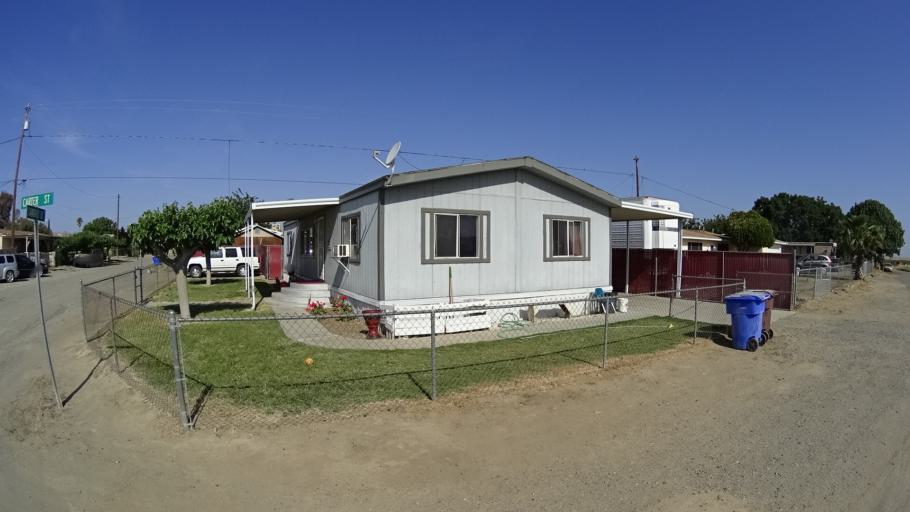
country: US
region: California
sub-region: Kings County
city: Kettleman City
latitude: 36.0093
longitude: -119.9577
